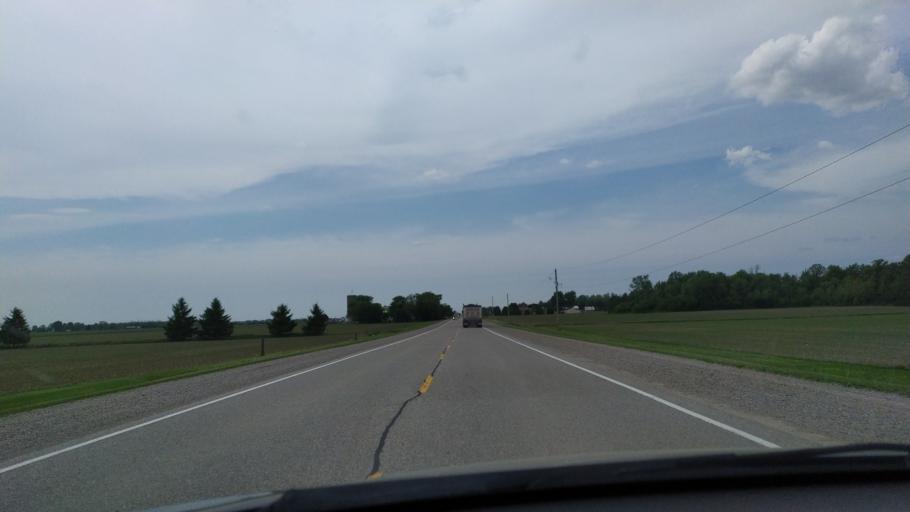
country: CA
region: Ontario
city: Stratford
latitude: 43.2369
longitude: -81.0795
